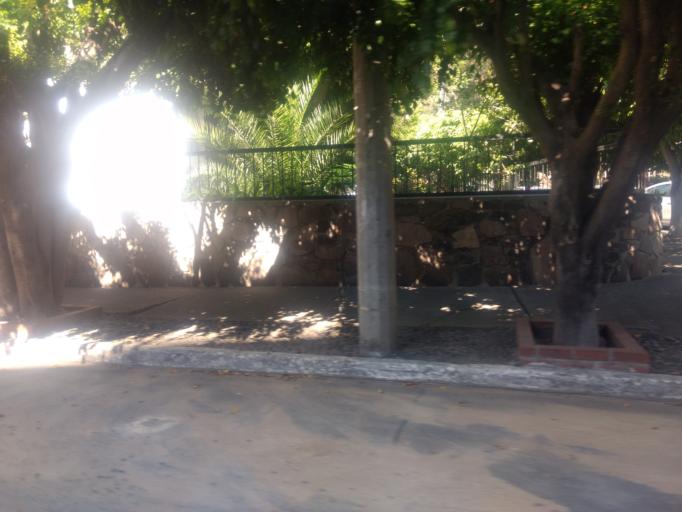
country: MX
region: Jalisco
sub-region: Zapopan
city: Zapopan
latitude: 20.6981
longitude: -103.3788
